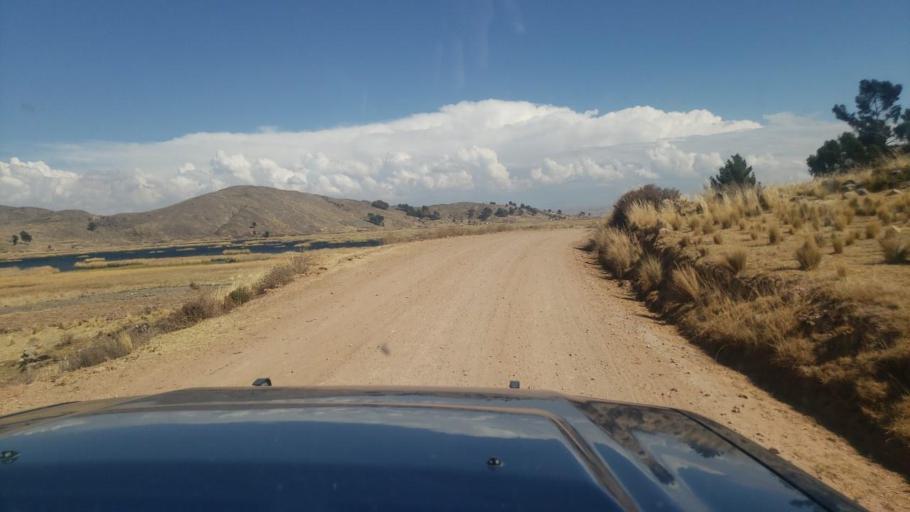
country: BO
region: La Paz
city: Huatajata
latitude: -16.3382
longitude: -68.6824
